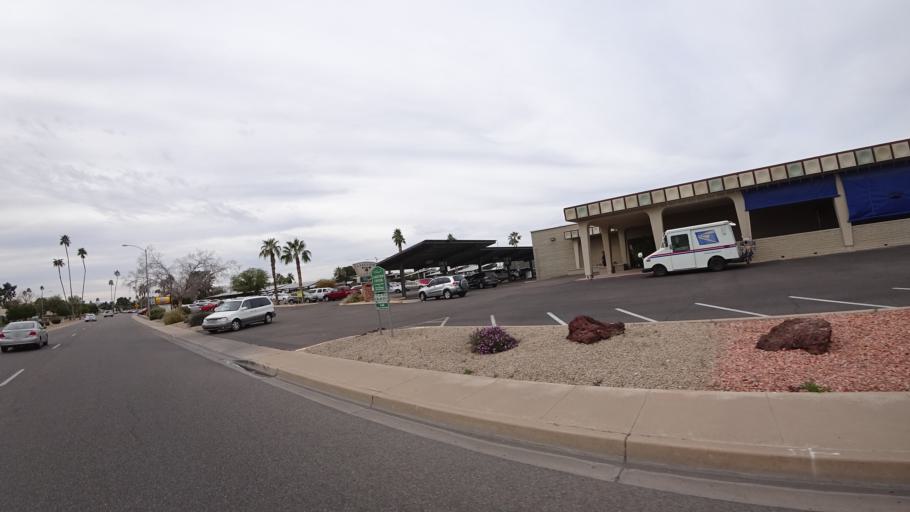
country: US
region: Arizona
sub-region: Maricopa County
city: Sun City
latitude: 33.6051
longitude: -112.2862
